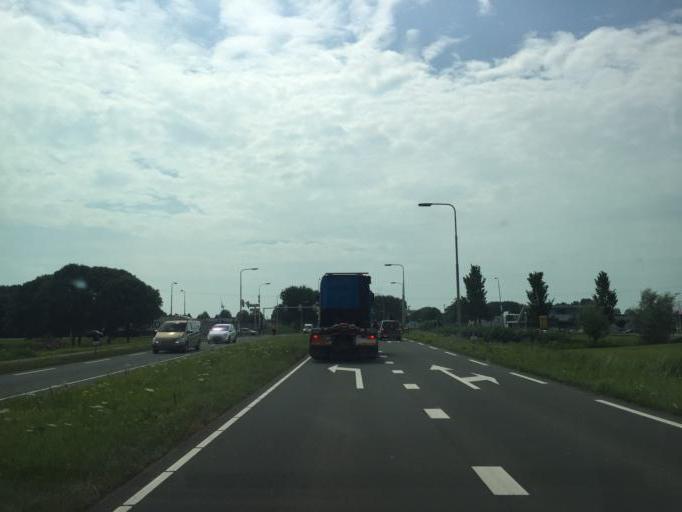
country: NL
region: North Holland
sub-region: Gemeente Enkhuizen
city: Enkhuizen
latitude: 52.6969
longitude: 5.2739
